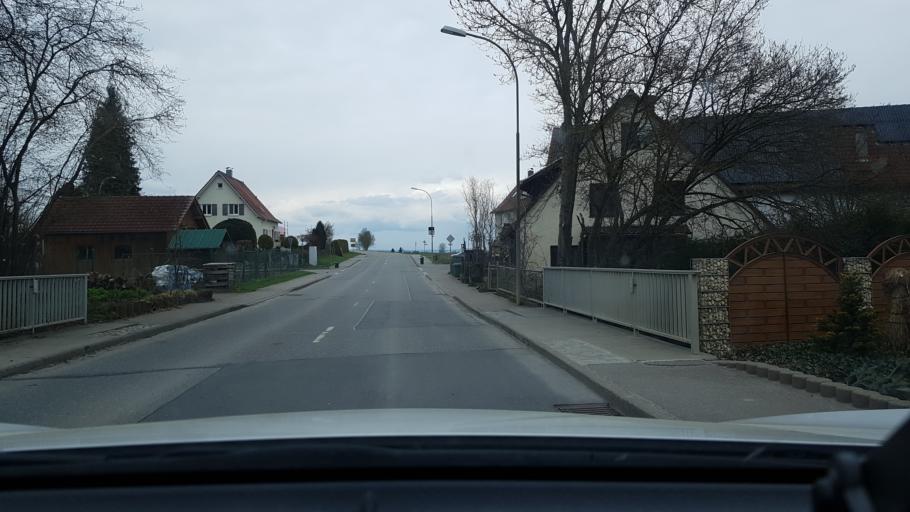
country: DE
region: Baden-Wuerttemberg
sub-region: Tuebingen Region
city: Oberstadion
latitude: 48.1799
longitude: 9.7239
